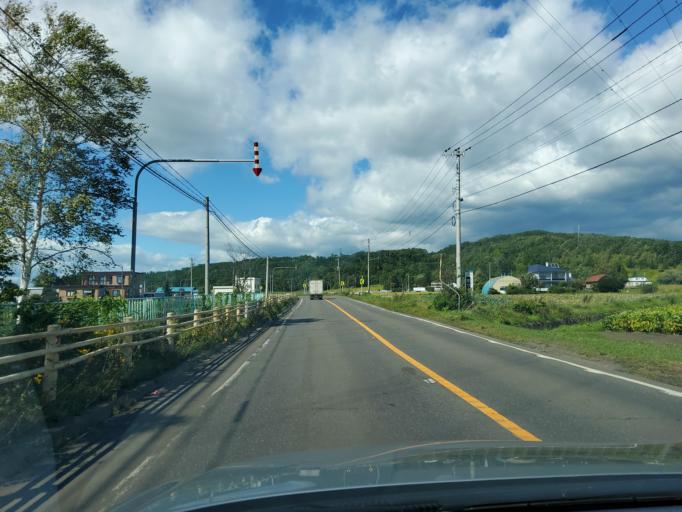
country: JP
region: Hokkaido
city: Obihiro
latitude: 42.9430
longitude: 143.2782
